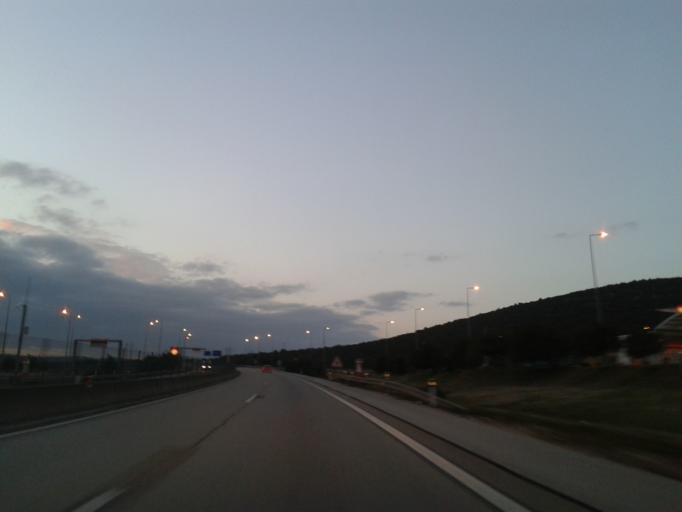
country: PT
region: Faro
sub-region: Loule
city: Boliqueime
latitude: 37.1365
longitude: -8.1101
